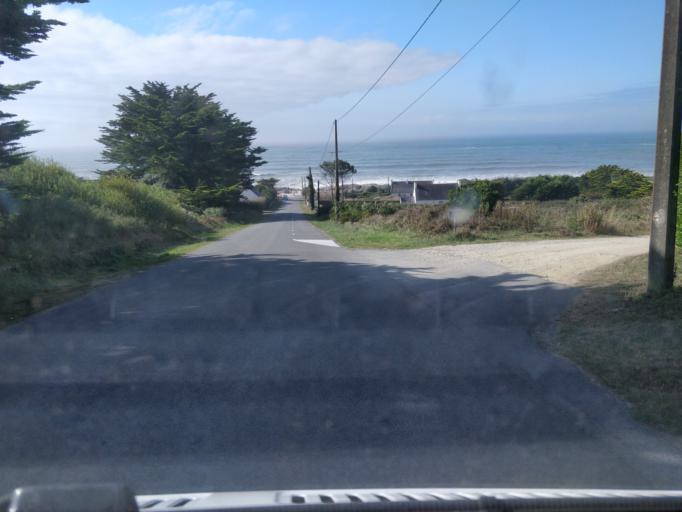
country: FR
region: Brittany
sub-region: Departement du Finistere
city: Plouhinec
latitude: 48.0038
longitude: -4.4972
